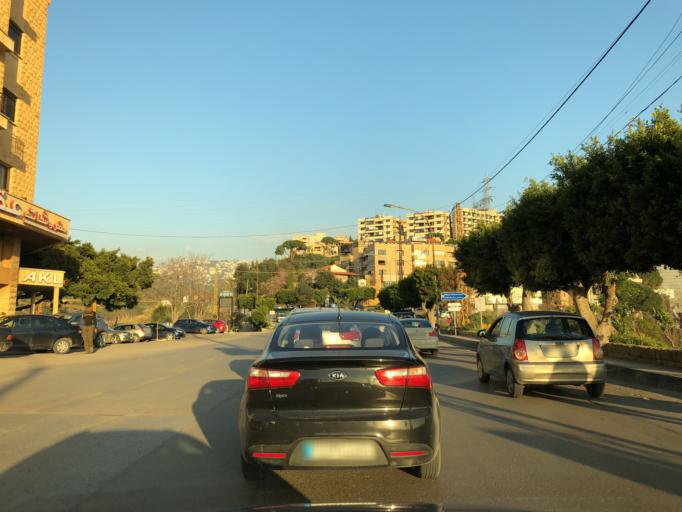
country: LB
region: Mont-Liban
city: Baabda
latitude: 33.8599
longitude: 35.5566
